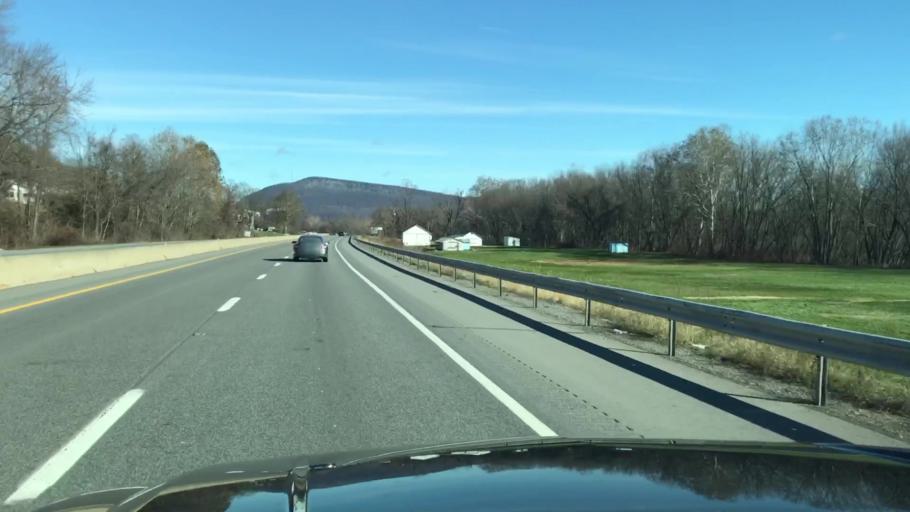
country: US
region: Pennsylvania
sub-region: Snyder County
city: Selinsgrove
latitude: 40.7028
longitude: -76.8689
